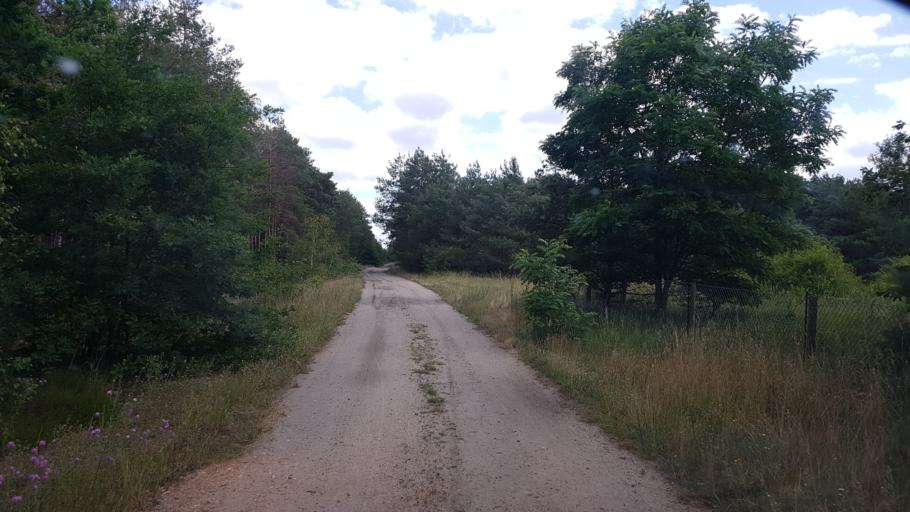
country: DE
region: Brandenburg
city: Finsterwalde
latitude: 51.6543
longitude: 13.7007
